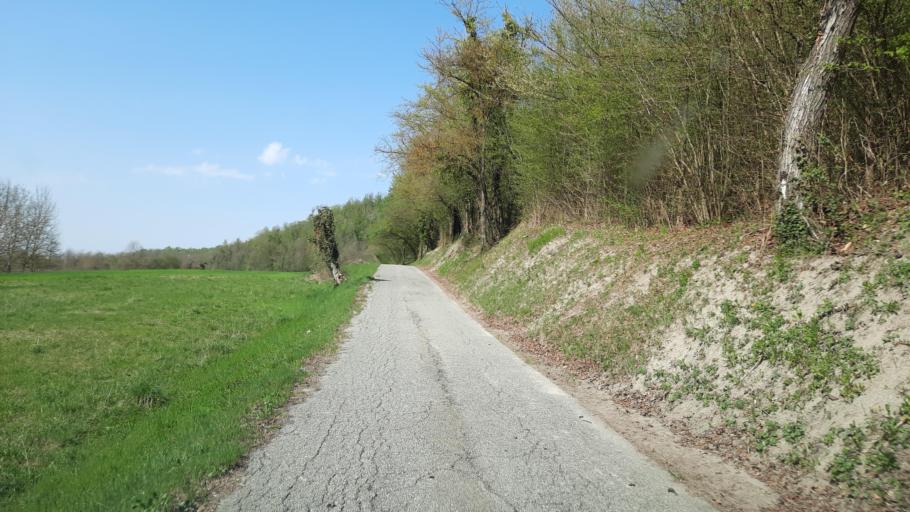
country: IT
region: Piedmont
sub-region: Provincia di Alessandria
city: Villamiroglio
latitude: 45.1365
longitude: 8.1813
